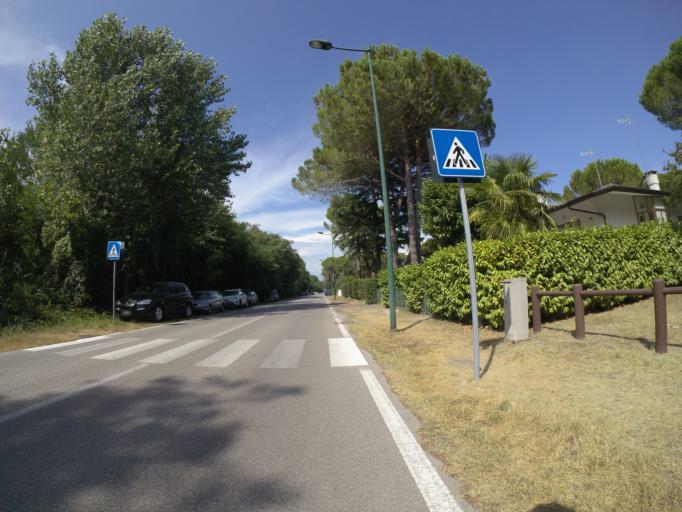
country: IT
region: Friuli Venezia Giulia
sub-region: Provincia di Udine
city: Lignano Sabbiadoro
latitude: 45.6563
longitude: 13.0947
